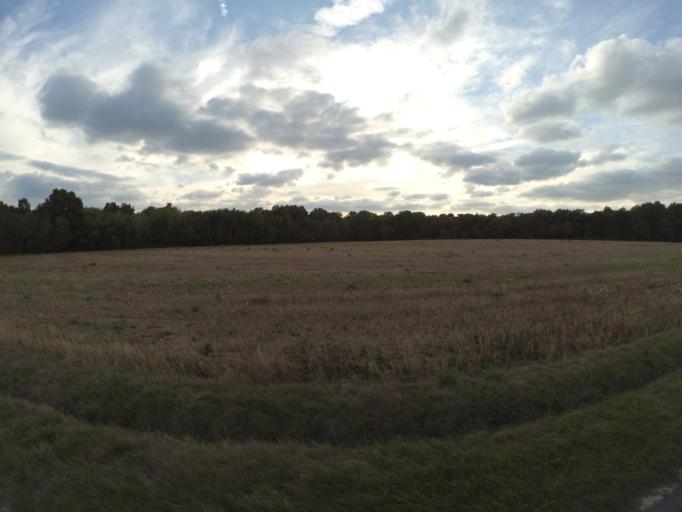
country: FR
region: Centre
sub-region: Departement d'Indre-et-Loire
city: Nazelles-Negron
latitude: 47.4595
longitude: 0.9631
